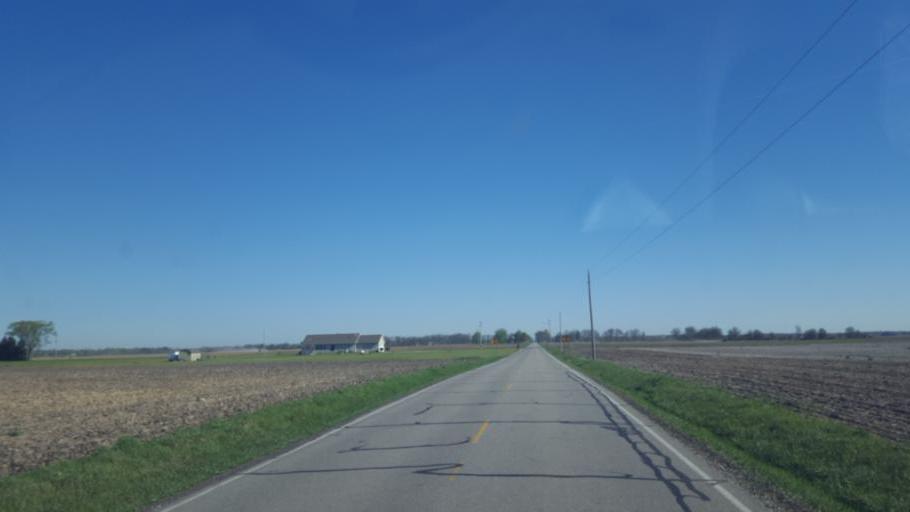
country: US
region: Ohio
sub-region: Marion County
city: Marion
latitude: 40.7151
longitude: -83.0923
